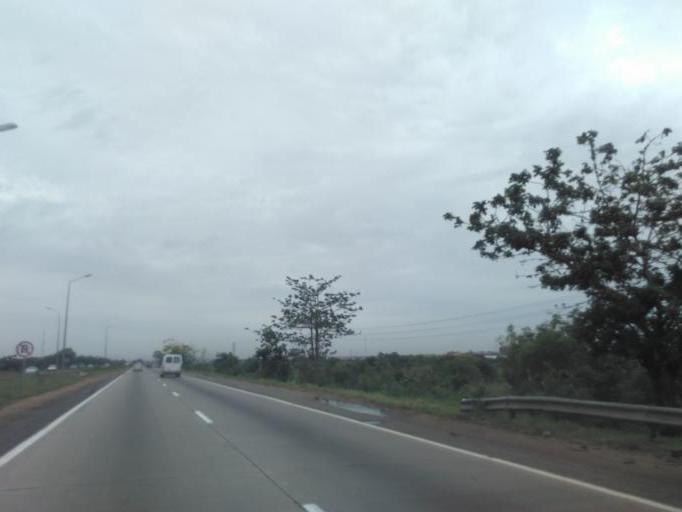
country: GH
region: Greater Accra
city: Nungua
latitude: 5.6569
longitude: -0.0885
